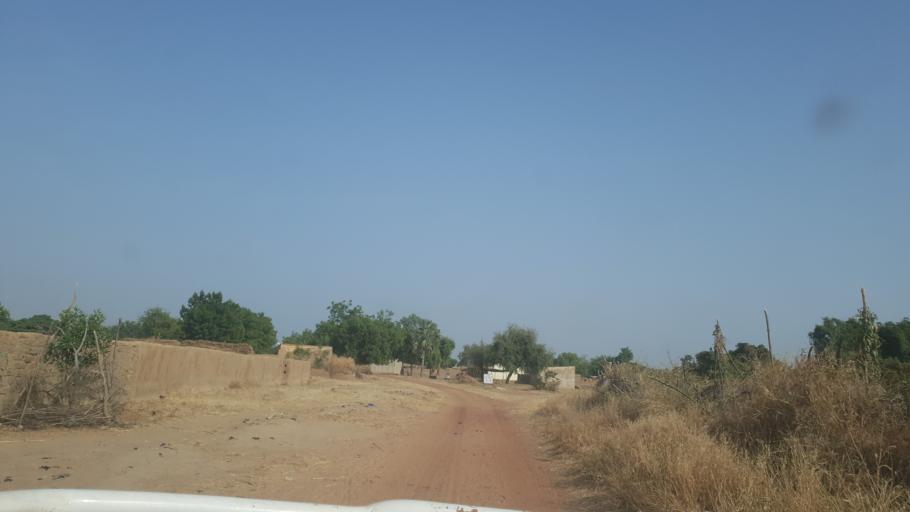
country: ML
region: Segou
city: Baroueli
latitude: 13.3532
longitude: -6.9339
